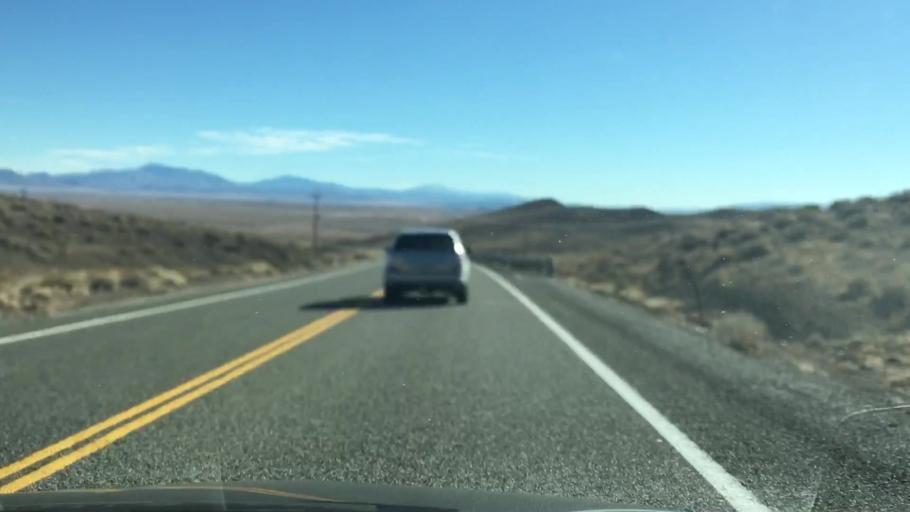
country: US
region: Nevada
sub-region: Lyon County
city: Yerington
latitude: 39.1734
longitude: -119.2051
